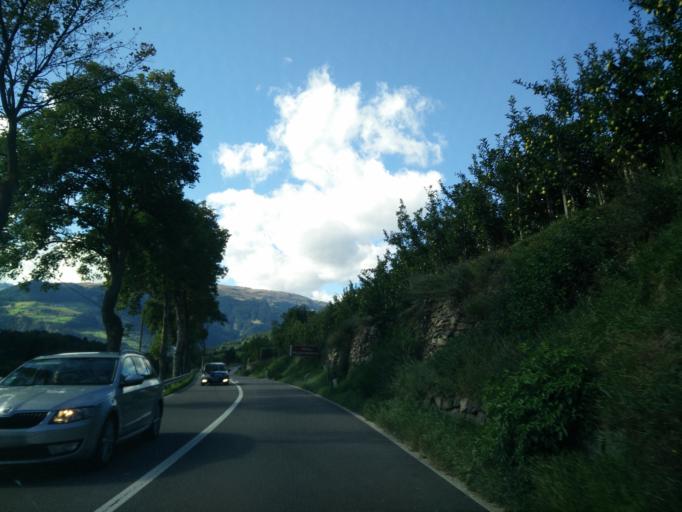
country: IT
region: Trentino-Alto Adige
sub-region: Bolzano
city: Sluderno
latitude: 46.6745
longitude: 10.5749
